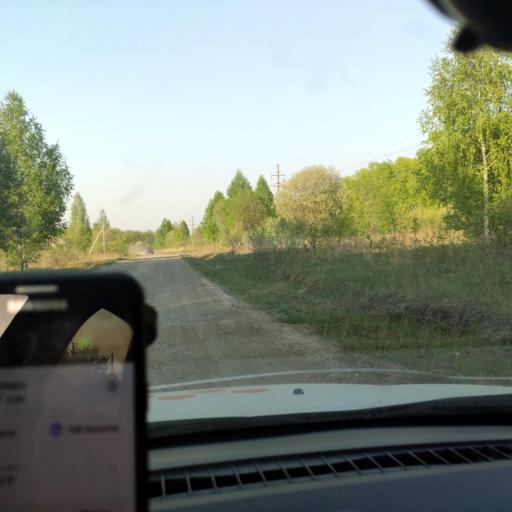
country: RU
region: Bashkortostan
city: Iglino
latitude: 54.7291
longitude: 56.2320
